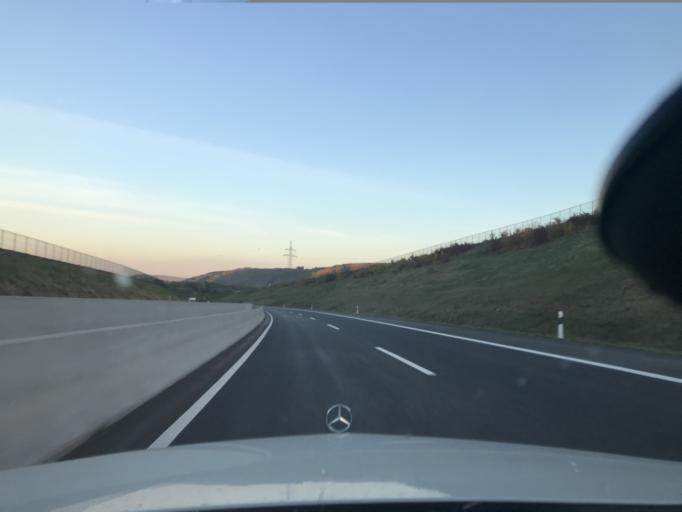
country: DE
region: Hesse
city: Waldkappel
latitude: 51.1568
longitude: 9.8571
